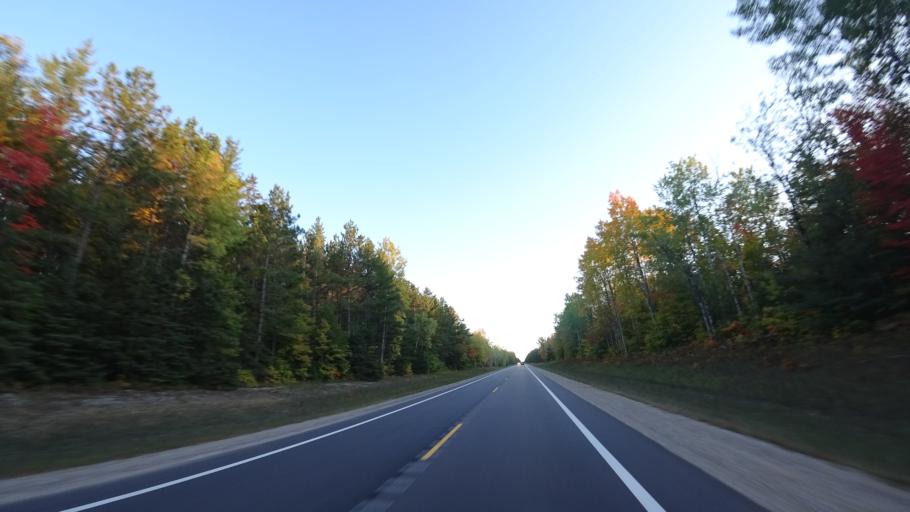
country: US
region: Michigan
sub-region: Luce County
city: Newberry
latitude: 46.3115
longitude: -85.0094
